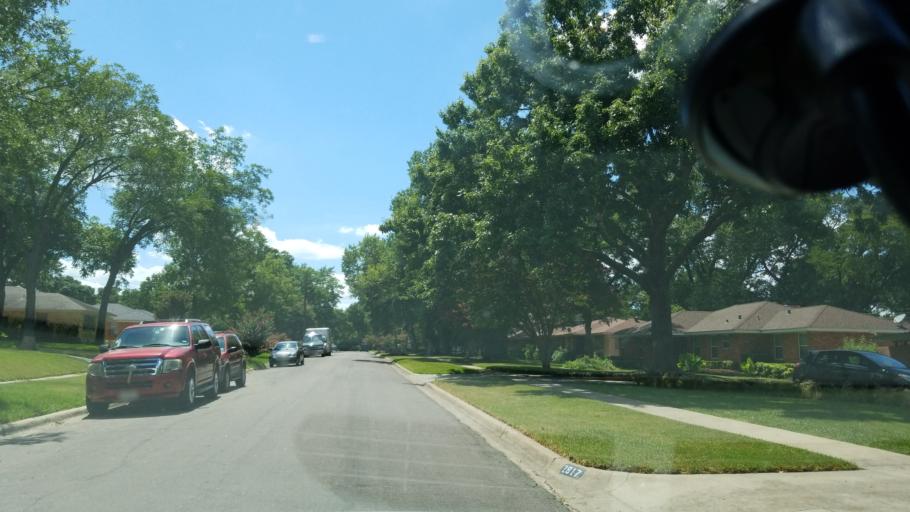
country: US
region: Texas
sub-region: Dallas County
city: Cockrell Hill
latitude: 32.7011
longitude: -96.8664
